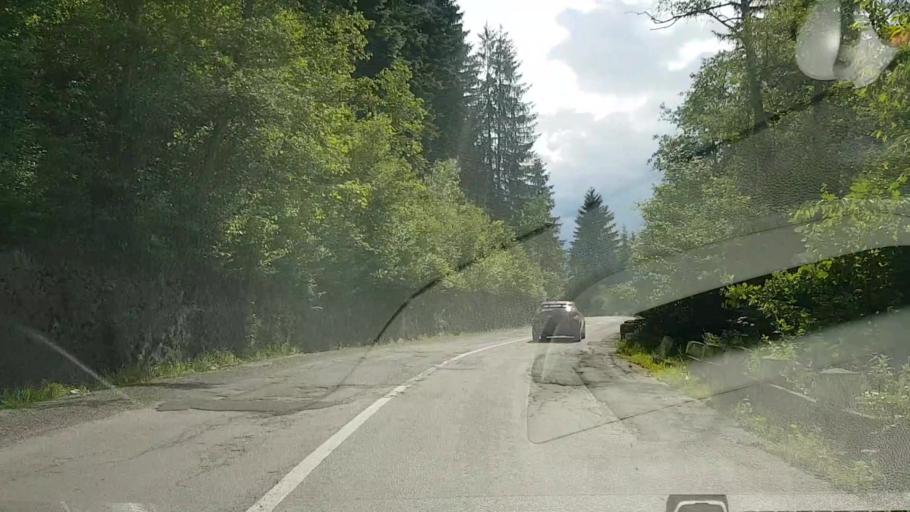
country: RO
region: Neamt
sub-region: Comuna Hangu
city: Hangu
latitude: 47.0154
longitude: 26.0843
